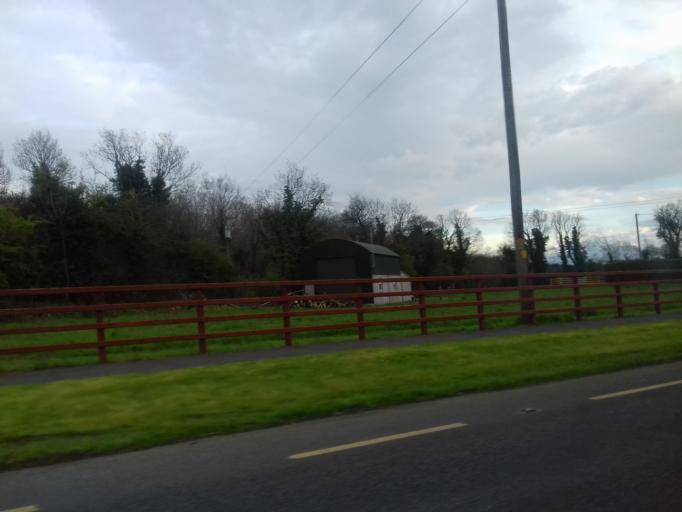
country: IE
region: Ulster
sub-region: An Cabhan
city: Belturbet
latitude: 54.0968
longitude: -7.4635
